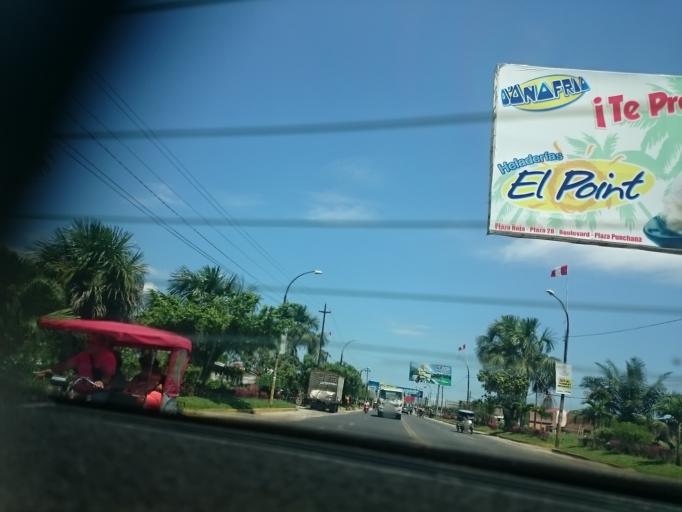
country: PE
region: Loreto
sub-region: Provincia de Maynas
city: Iquitos
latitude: -3.7828
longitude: -73.2973
